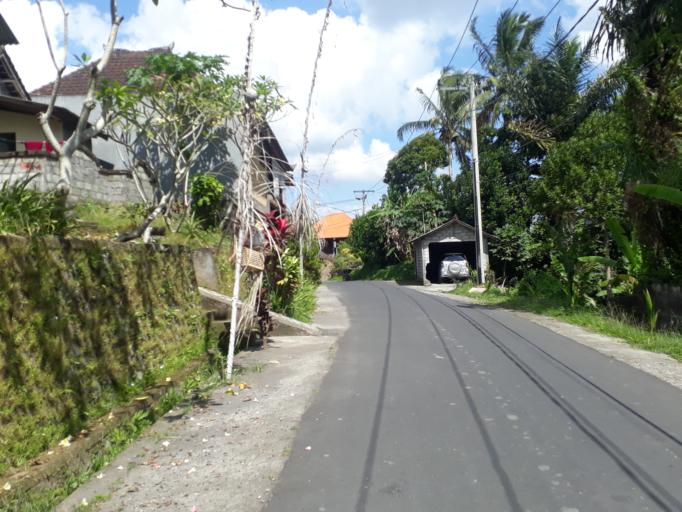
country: ID
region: Bali
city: Banjar Wangsian
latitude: -8.4703
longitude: 115.4438
